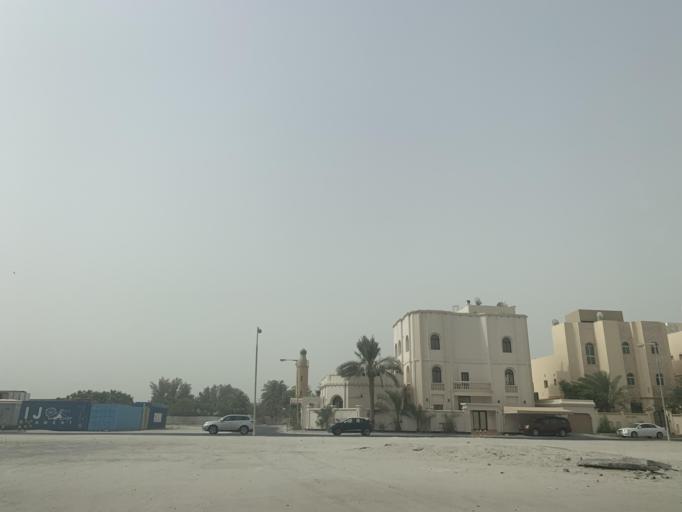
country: BH
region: Manama
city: Jidd Hafs
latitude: 26.2249
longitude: 50.5549
